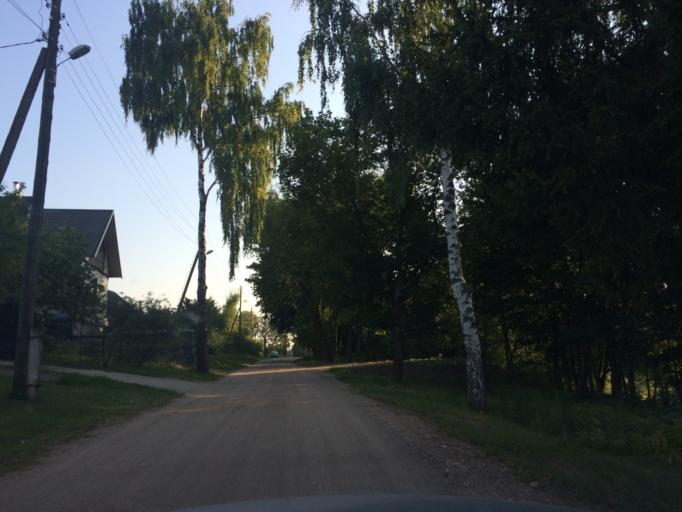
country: LV
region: Rezekne
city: Rezekne
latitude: 56.5099
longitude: 27.3526
